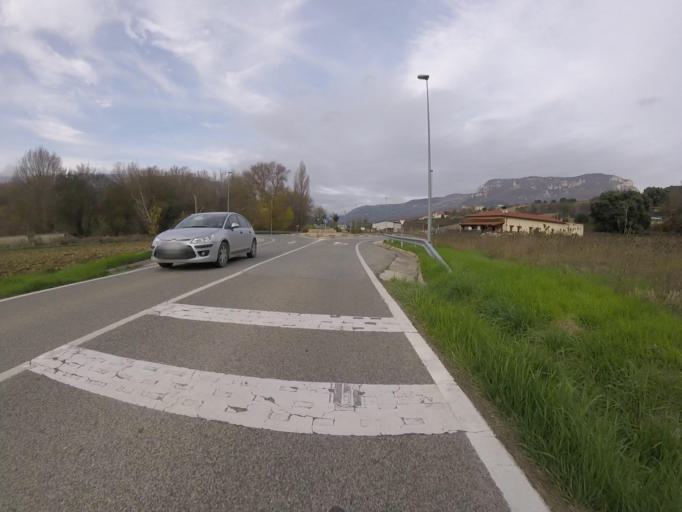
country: ES
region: Navarre
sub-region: Provincia de Navarra
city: Estella
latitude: 42.7137
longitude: -2.0731
